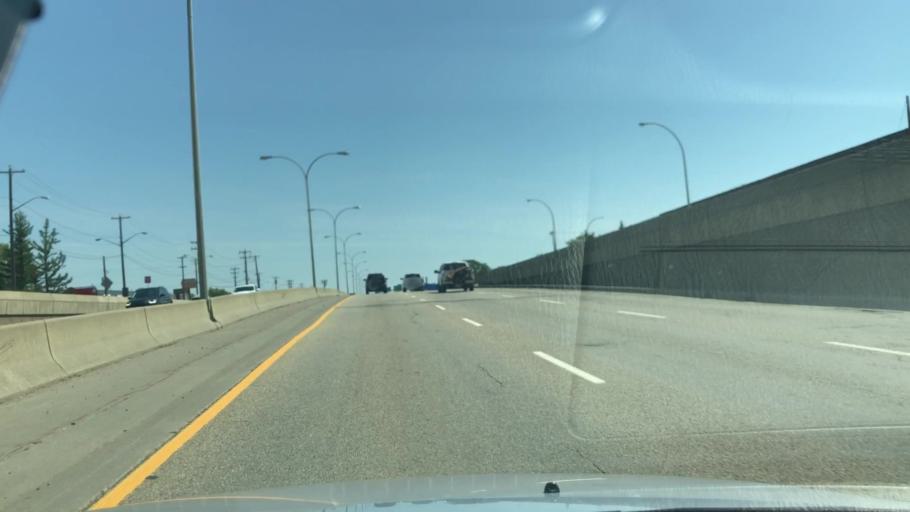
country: CA
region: Alberta
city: Edmonton
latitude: 53.5822
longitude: -113.4655
